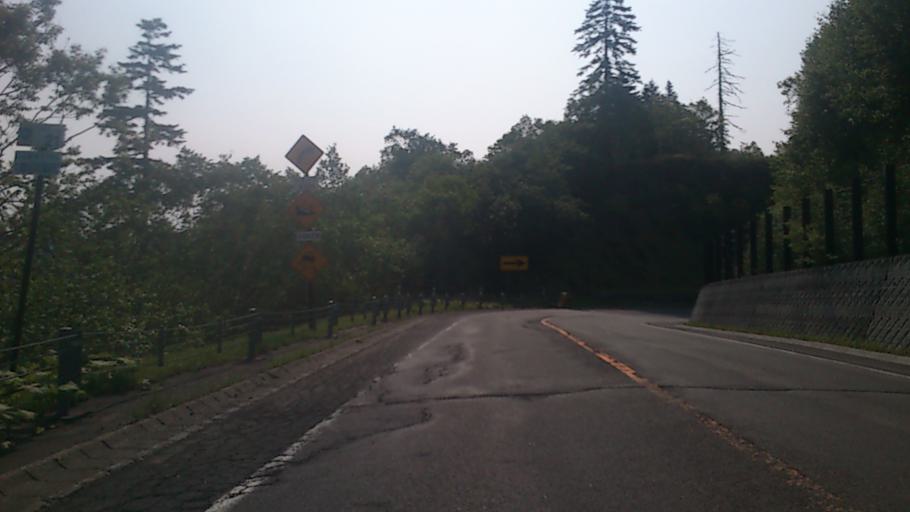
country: JP
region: Hokkaido
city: Bihoro
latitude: 43.4606
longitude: 144.2446
